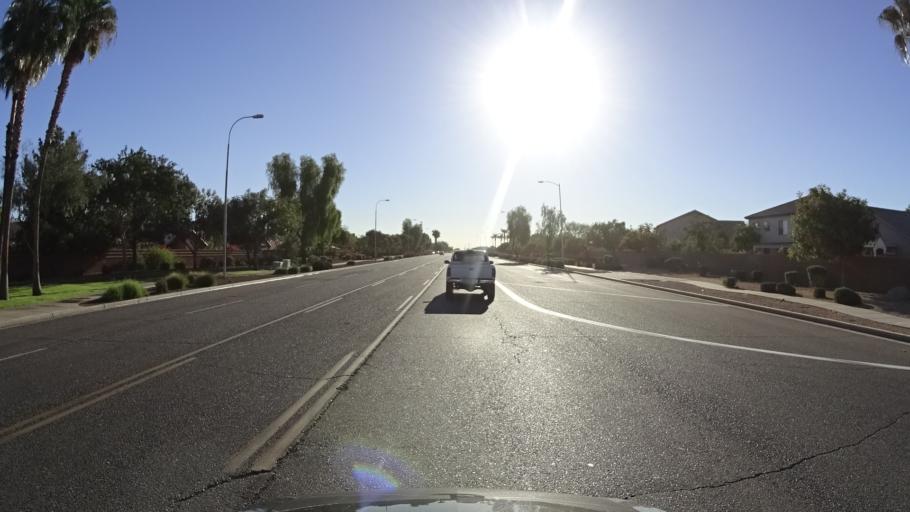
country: US
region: Arizona
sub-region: Maricopa County
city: Tolleson
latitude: 33.4230
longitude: -112.2336
